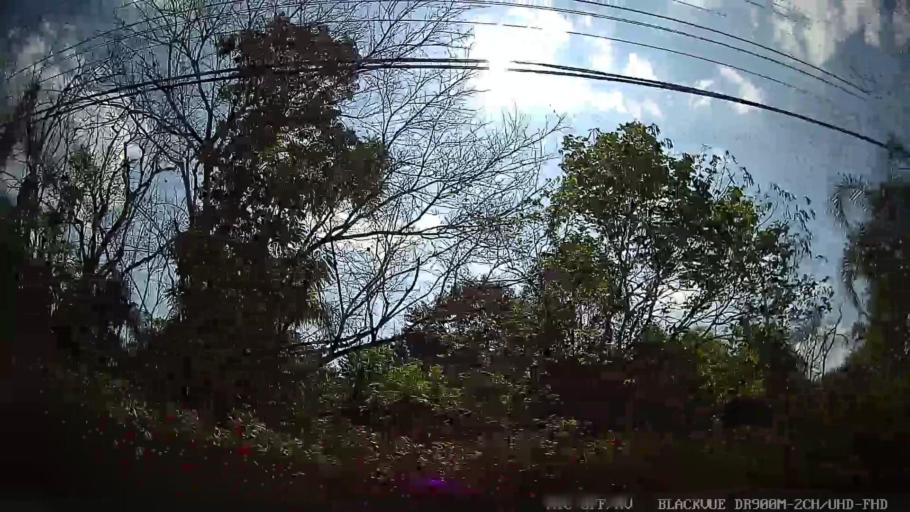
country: BR
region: Sao Paulo
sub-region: Itupeva
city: Itupeva
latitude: -23.2145
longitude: -47.0796
